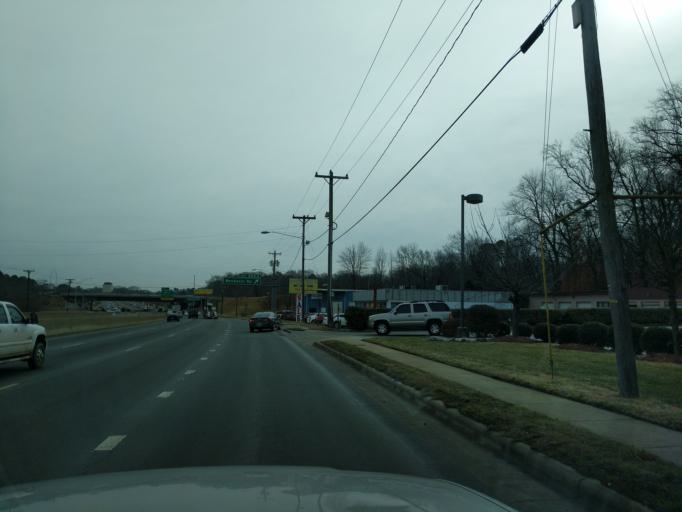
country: US
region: North Carolina
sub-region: Mecklenburg County
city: Charlotte
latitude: 35.2025
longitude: -80.7900
